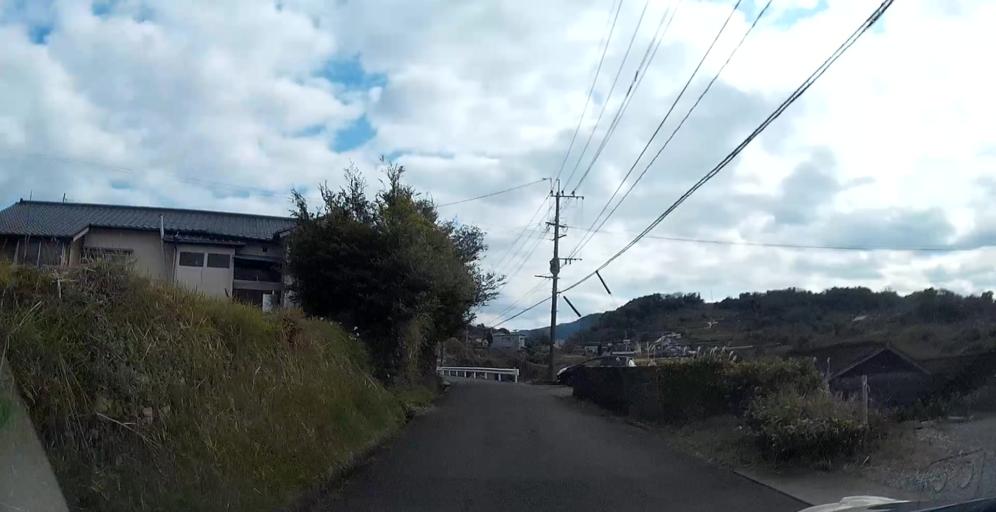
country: JP
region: Kumamoto
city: Minamata
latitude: 32.2090
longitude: 130.3848
